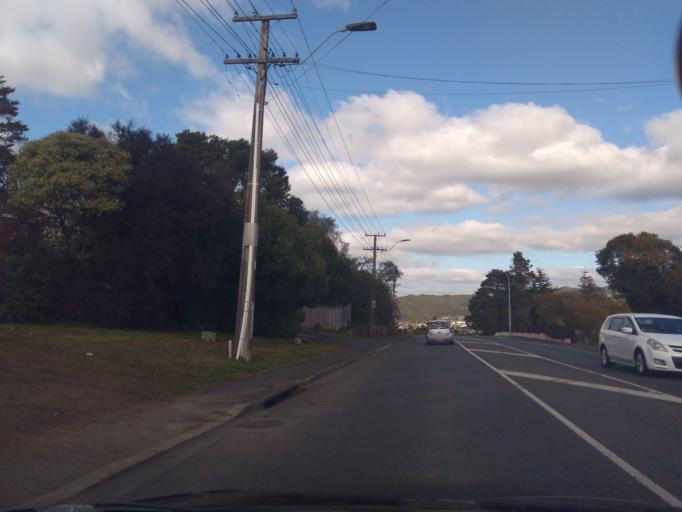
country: NZ
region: Northland
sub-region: Whangarei
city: Whangarei
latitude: -35.6936
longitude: 174.3263
